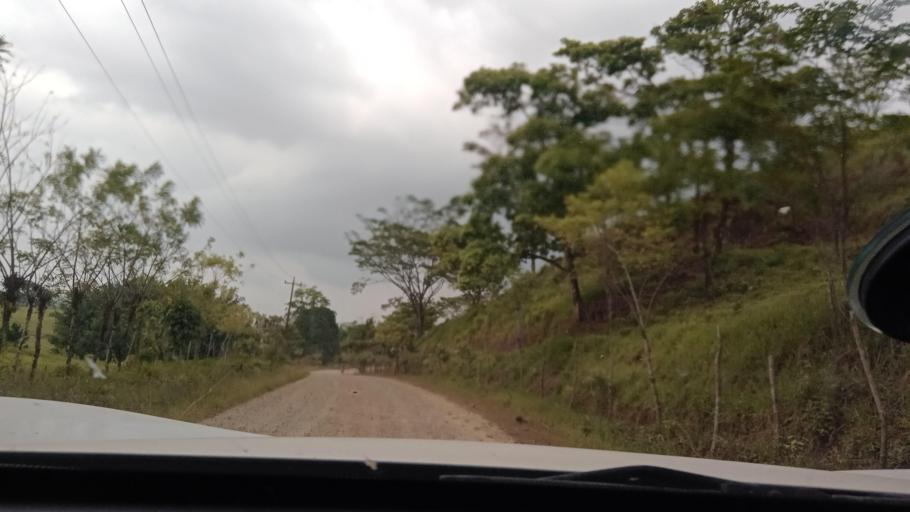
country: MX
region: Tabasco
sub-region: Huimanguillo
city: Francisco Rueda
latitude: 17.4336
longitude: -94.0481
